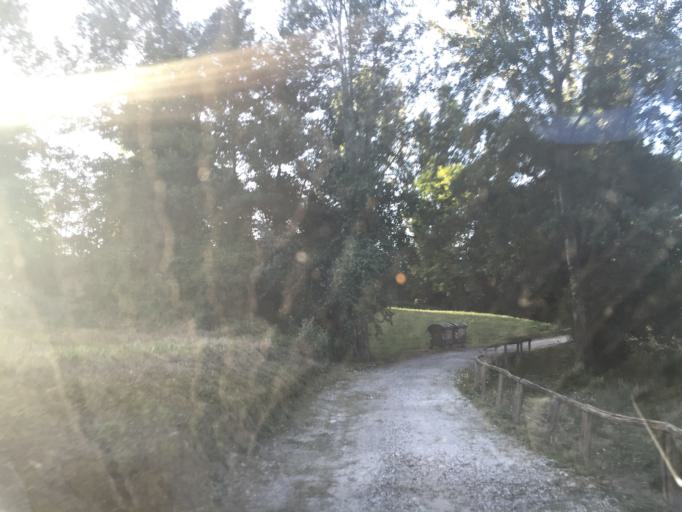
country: IT
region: Tuscany
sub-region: Provincia di Lucca
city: Castelnuovo di Garfagnana
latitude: 44.1199
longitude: 10.3908
